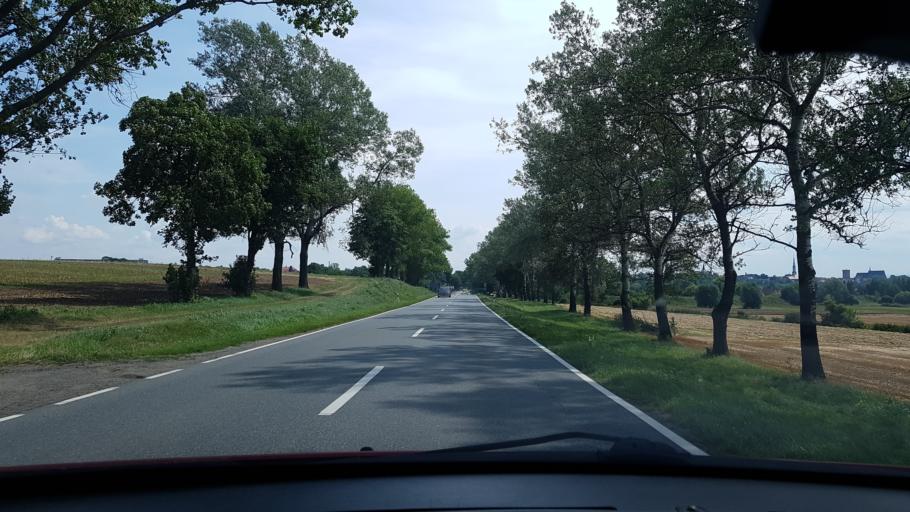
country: PL
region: Lower Silesian Voivodeship
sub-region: Powiat zabkowicki
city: Zabkowice Slaskie
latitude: 50.6023
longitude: 16.7990
